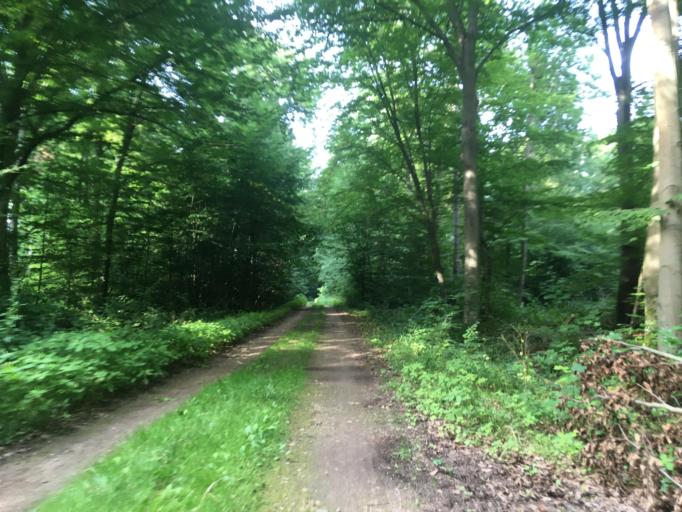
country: DE
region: Brandenburg
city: Eberswalde
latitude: 52.8155
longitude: 13.8193
